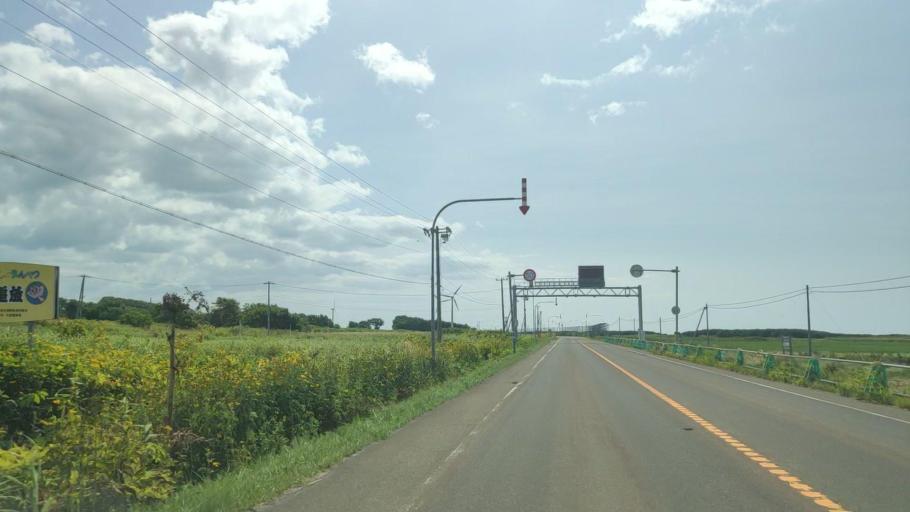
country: JP
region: Hokkaido
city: Makubetsu
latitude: 44.7125
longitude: 141.7907
